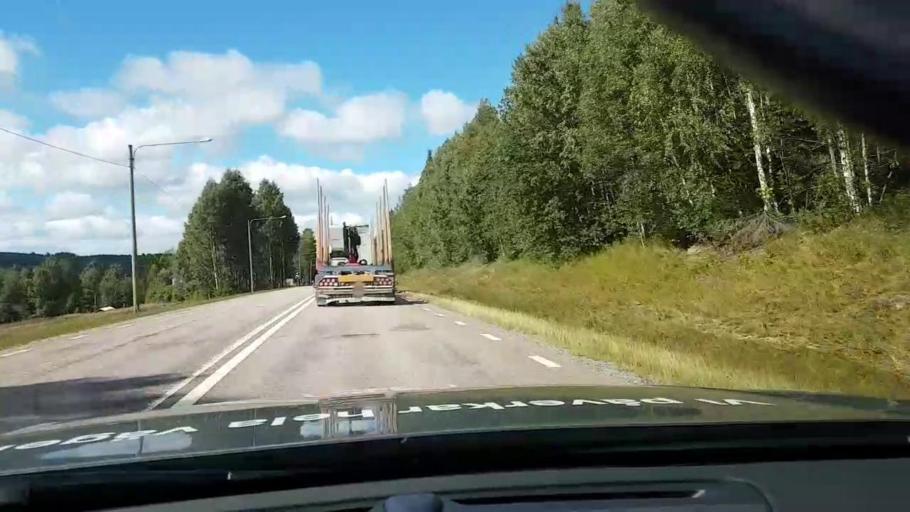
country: SE
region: Vaesternorrland
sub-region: OErnskoeldsviks Kommun
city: Bjasta
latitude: 63.3835
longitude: 18.3983
